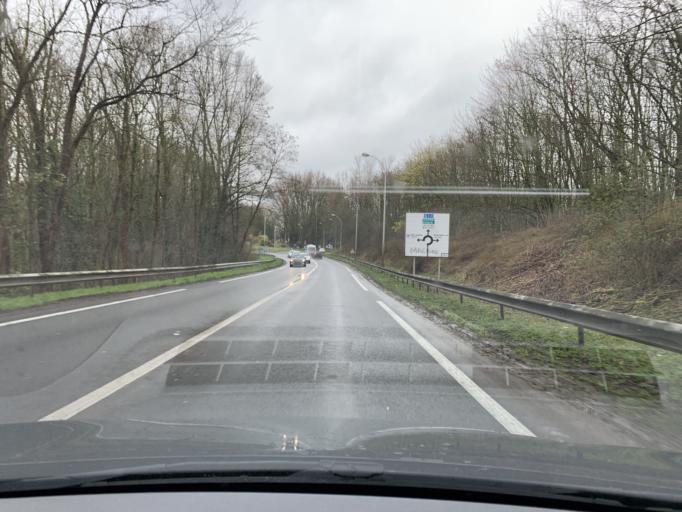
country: FR
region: Nord-Pas-de-Calais
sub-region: Departement du Nord
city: Sin-le-Noble
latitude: 50.3608
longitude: 3.1238
